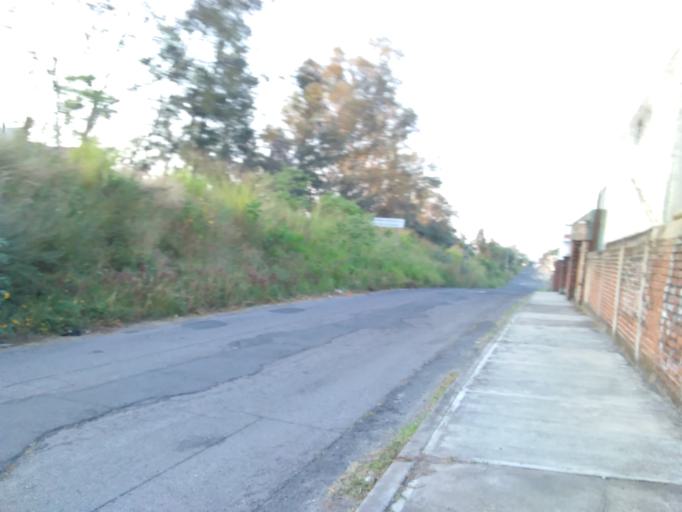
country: MX
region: Nayarit
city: Tepic
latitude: 21.5137
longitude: -104.9239
